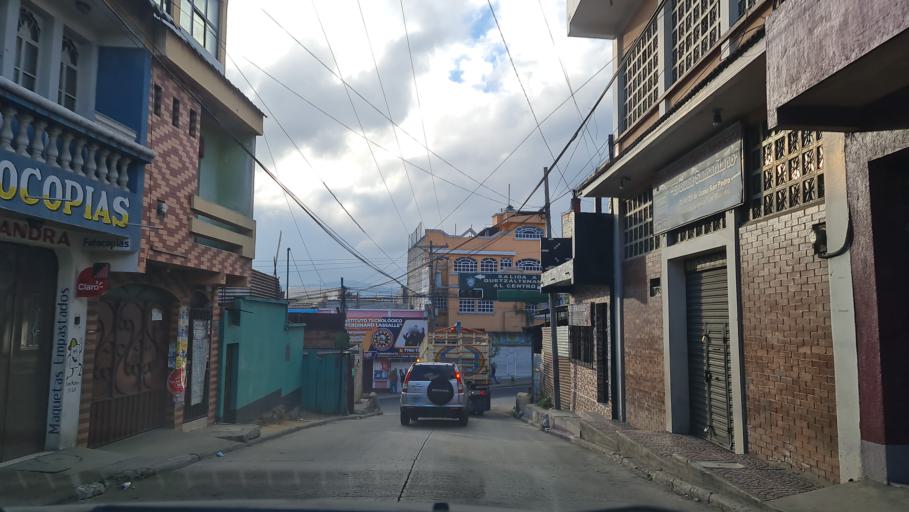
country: GT
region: San Marcos
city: San Pedro Sacatepequez
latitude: 14.9735
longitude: -91.7773
